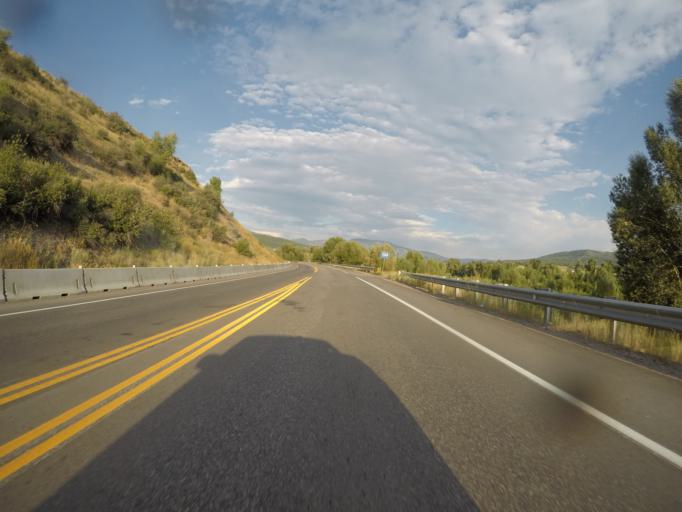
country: US
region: Colorado
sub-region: Routt County
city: Steamboat Springs
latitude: 40.5044
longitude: -106.8748
